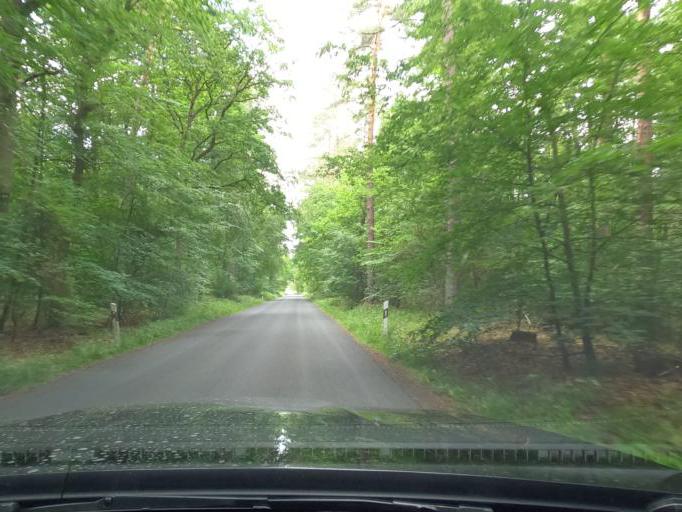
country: DE
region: Lower Saxony
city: Steimbke
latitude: 52.6385
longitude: 9.4634
